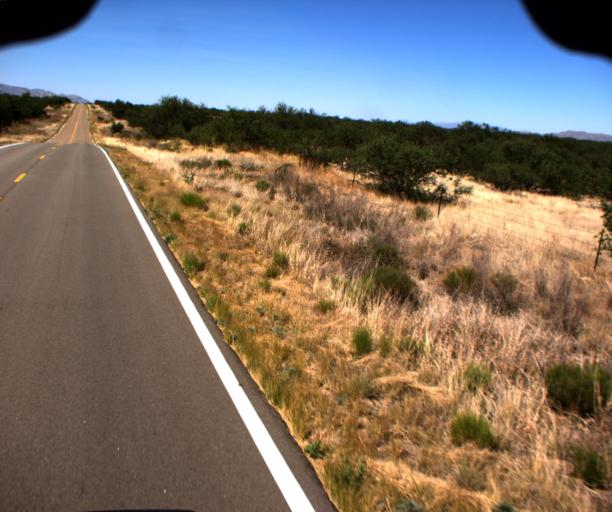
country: US
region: Arizona
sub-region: Santa Cruz County
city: Tubac
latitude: 31.5348
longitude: -111.5409
